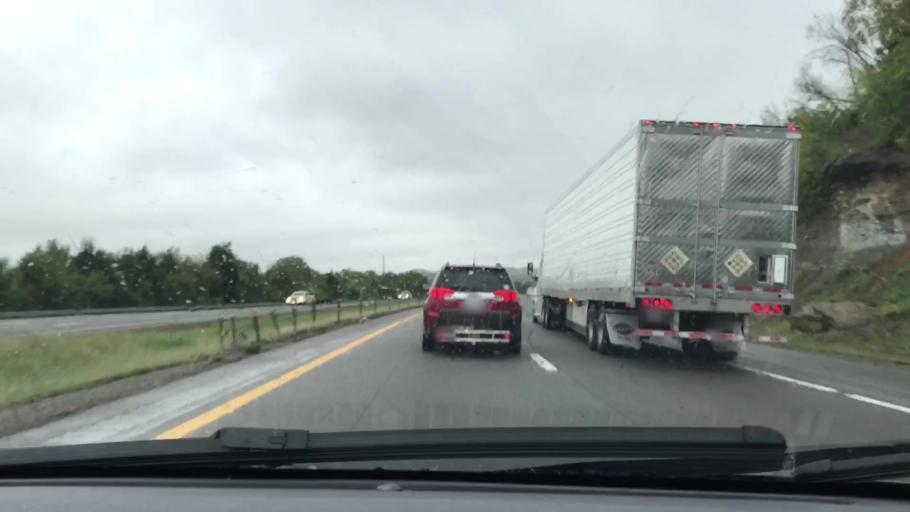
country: US
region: Tennessee
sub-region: Davidson County
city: Nashville
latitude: 36.2473
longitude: -86.7840
